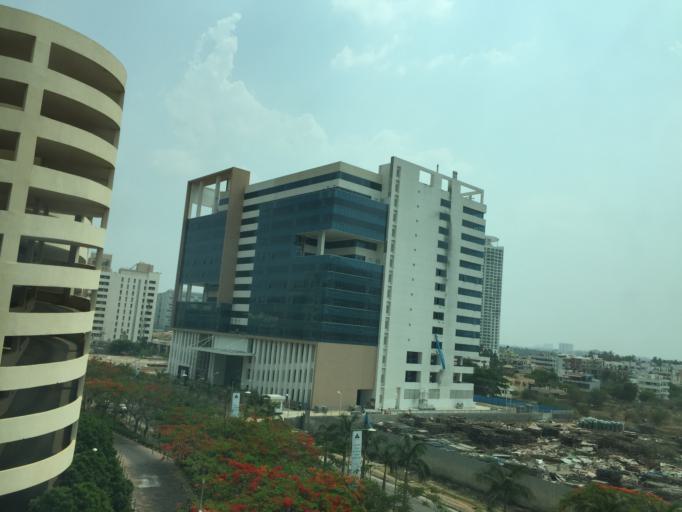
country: IN
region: Karnataka
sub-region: Bangalore Urban
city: Yelahanka
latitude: 13.0508
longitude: 77.6197
